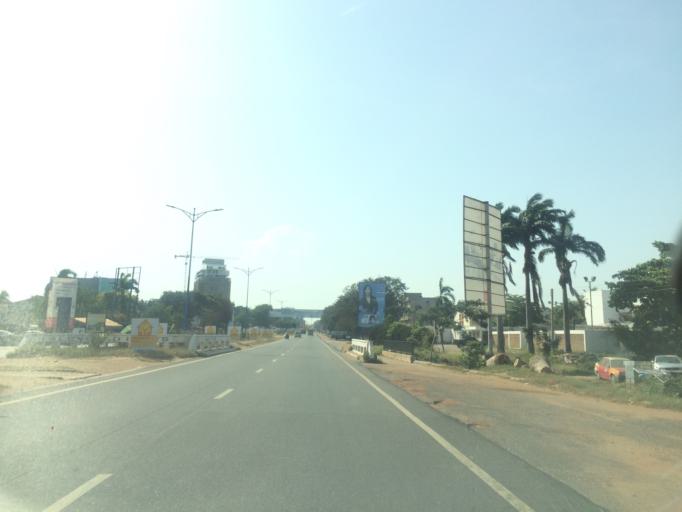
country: GH
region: Greater Accra
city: Accra
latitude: 5.5648
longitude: -0.1768
